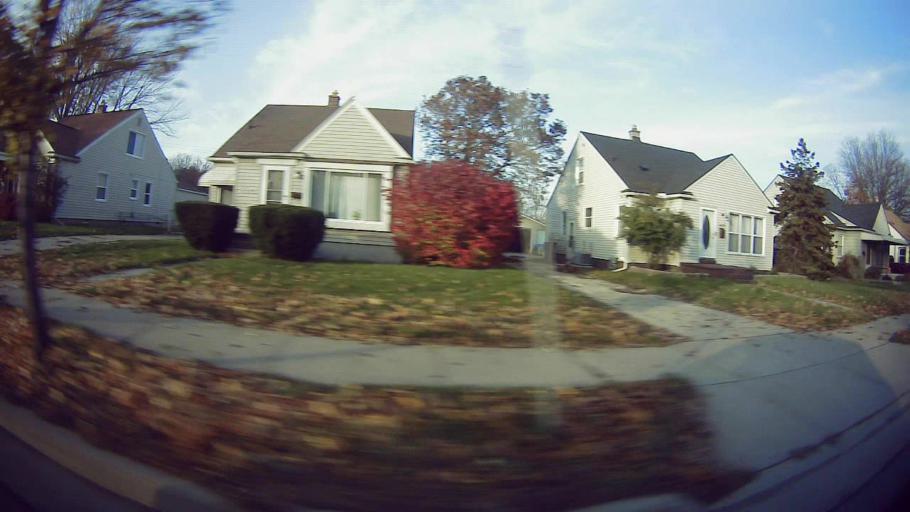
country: US
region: Michigan
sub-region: Oakland County
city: Clawson
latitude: 42.5195
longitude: -83.1279
